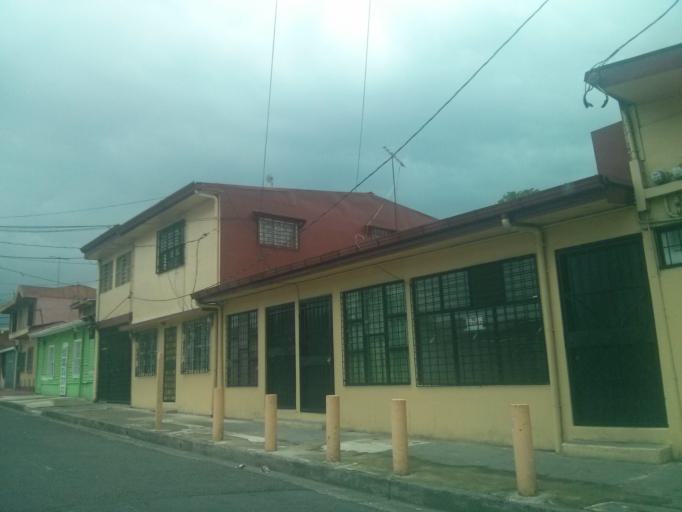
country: CR
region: San Jose
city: San Jose
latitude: 9.9246
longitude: -84.0686
